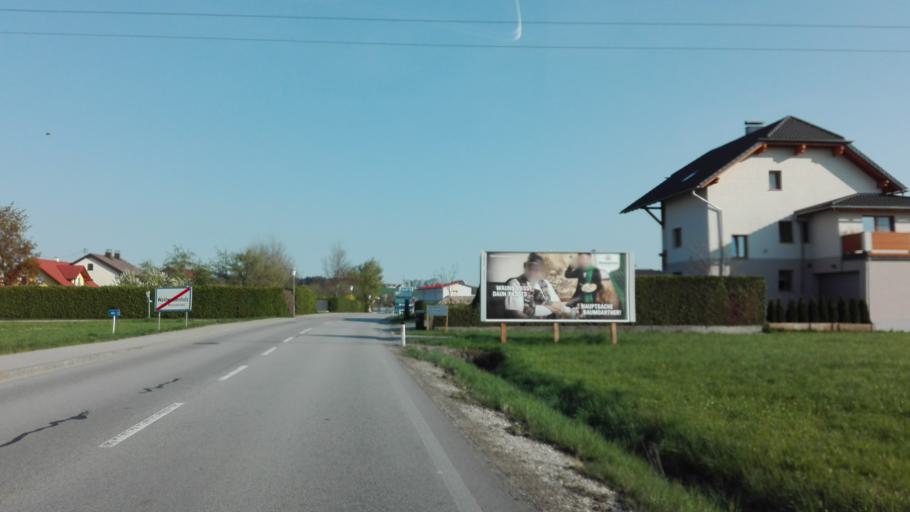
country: AT
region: Upper Austria
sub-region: Politischer Bezirk Grieskirchen
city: Grieskirchen
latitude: 48.3357
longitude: 13.8474
